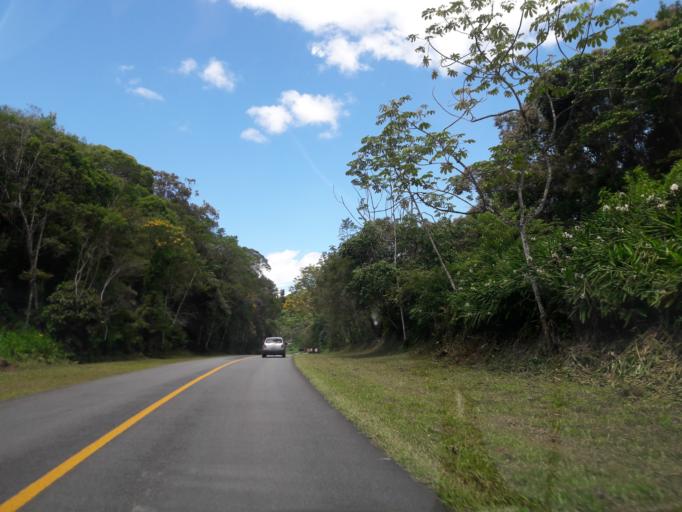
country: BR
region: Parana
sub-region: Antonina
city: Antonina
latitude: -25.4412
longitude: -48.7870
